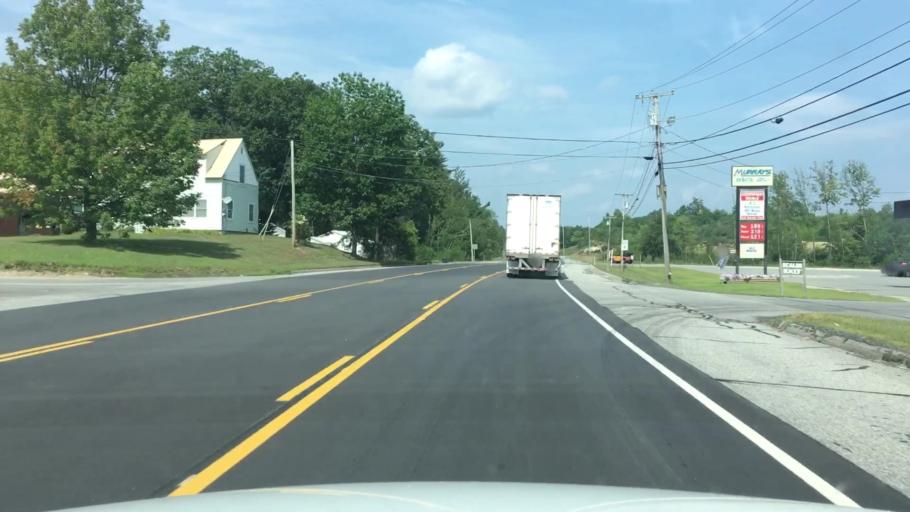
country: US
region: Maine
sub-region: Androscoggin County
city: Turner
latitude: 44.2701
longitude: -70.2684
